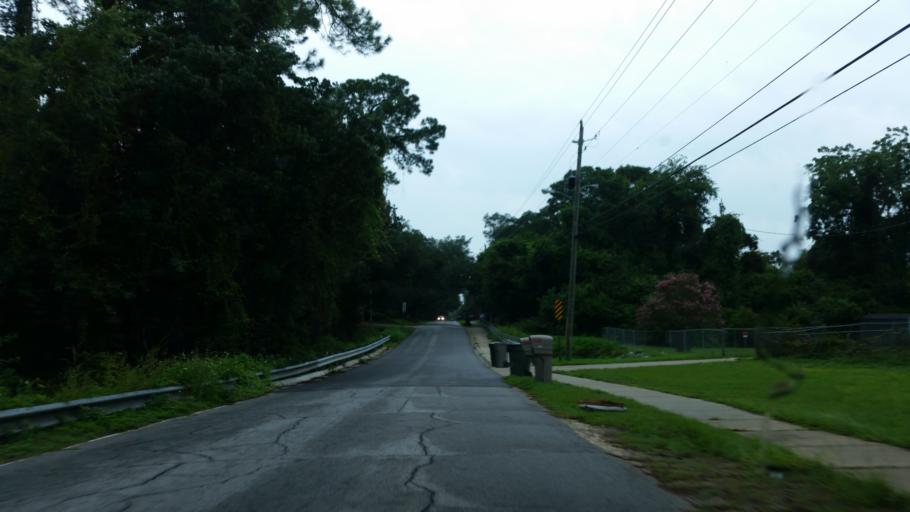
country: US
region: Florida
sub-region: Escambia County
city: Warrington
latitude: 30.3862
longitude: -87.2835
